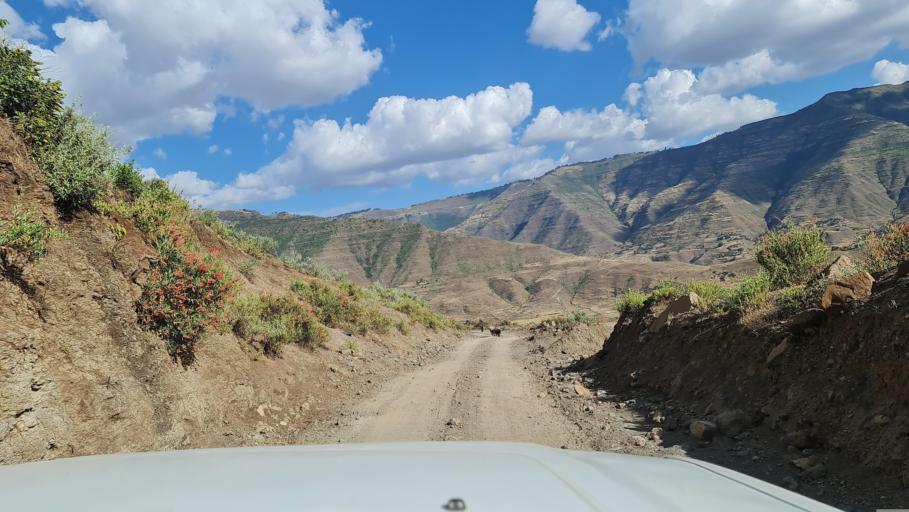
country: ET
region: Amhara
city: Debark'
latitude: 13.1194
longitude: 38.0204
